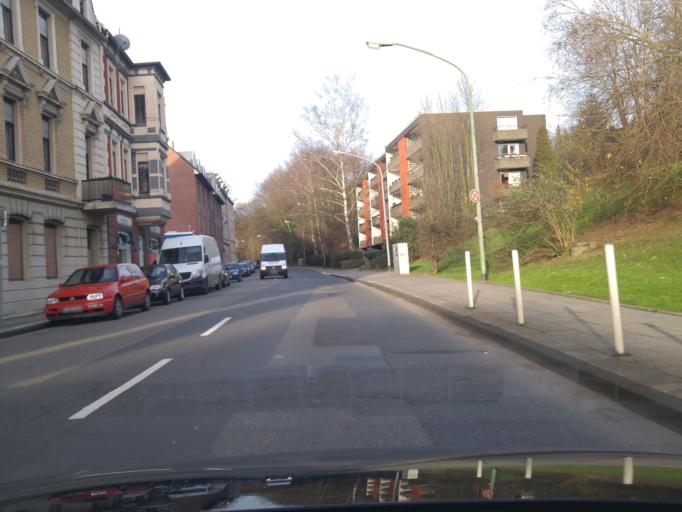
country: DE
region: North Rhine-Westphalia
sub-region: Regierungsbezirk Dusseldorf
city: Velbert
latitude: 51.3981
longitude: 7.0858
